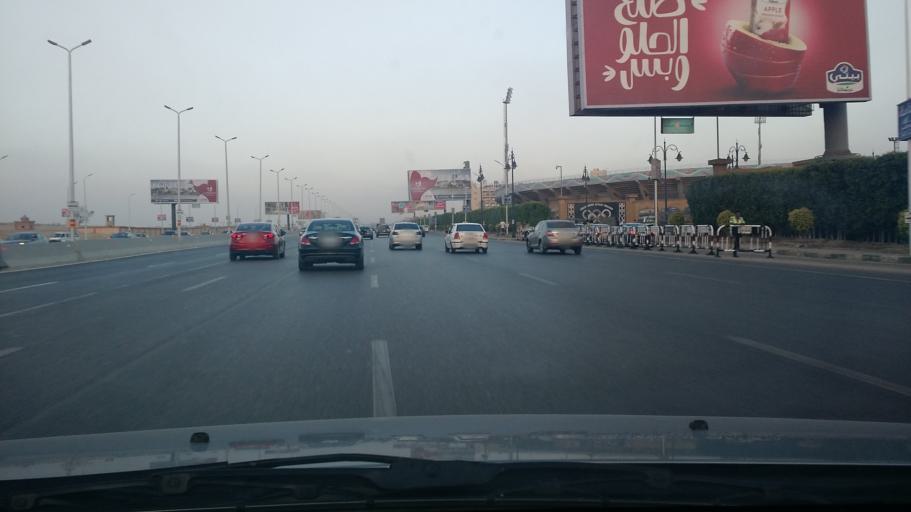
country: EG
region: Muhafazat al Qahirah
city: Cairo
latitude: 30.0221
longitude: 31.3714
